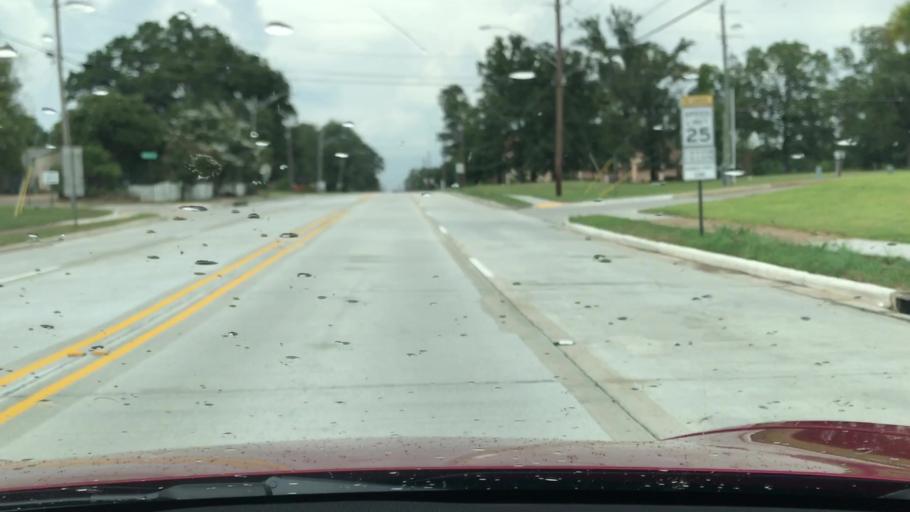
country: US
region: Louisiana
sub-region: Bossier Parish
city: Bossier City
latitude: 32.4052
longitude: -93.7633
